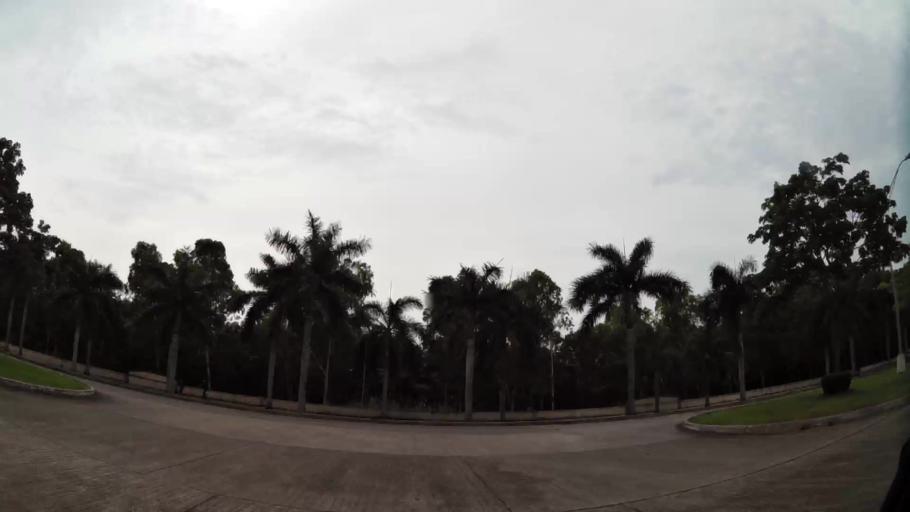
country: PA
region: Panama
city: San Miguelito
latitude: 9.0108
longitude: -79.4599
